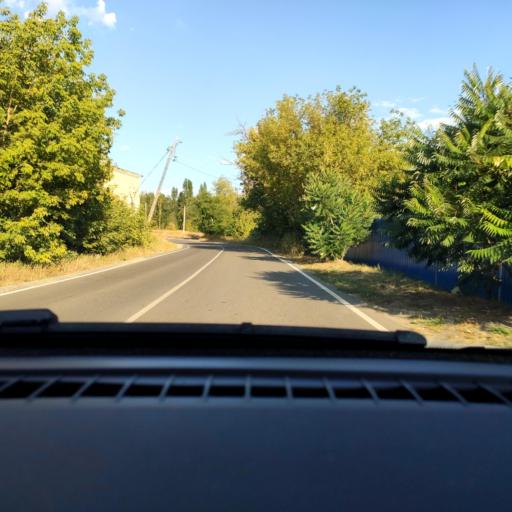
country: RU
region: Voronezj
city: Devitsa
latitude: 51.6539
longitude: 38.9817
